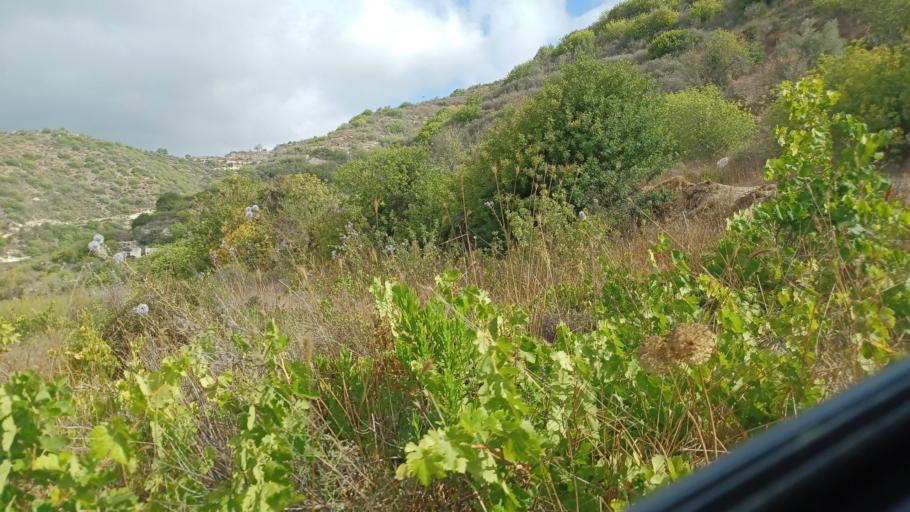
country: CY
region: Pafos
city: Tala
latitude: 34.8730
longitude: 32.4586
